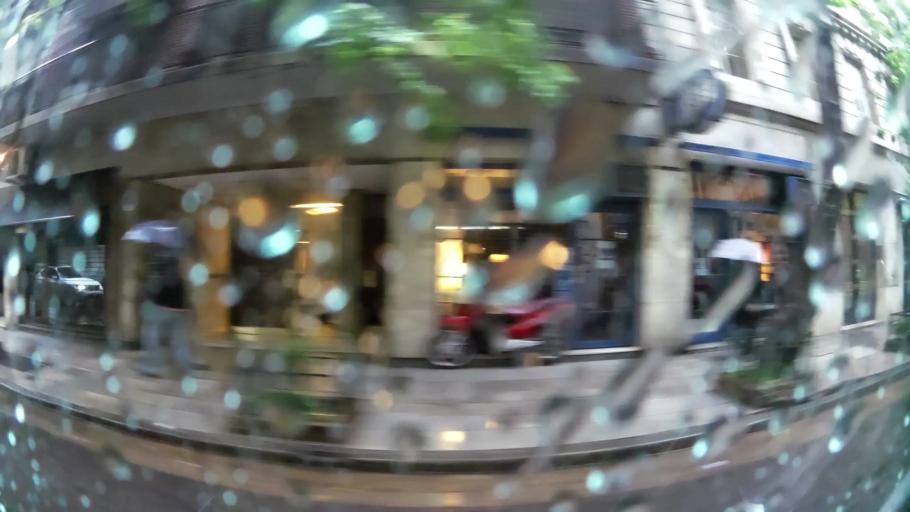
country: AR
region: Buenos Aires F.D.
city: Retiro
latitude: -34.5927
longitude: -58.3859
